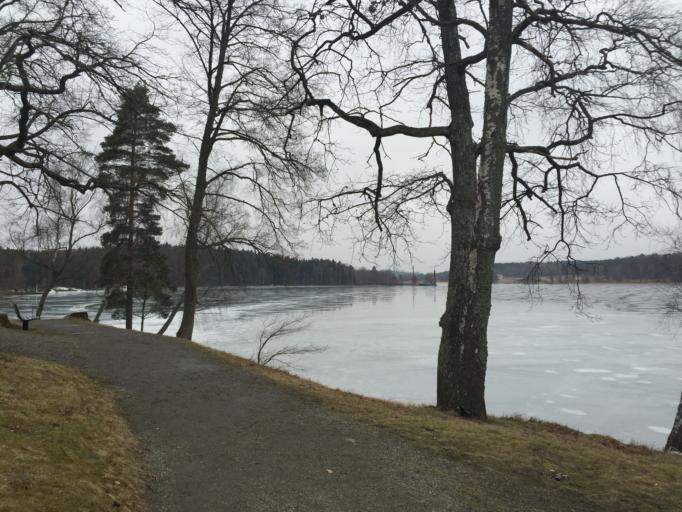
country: SE
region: Soedermanland
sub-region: Strangnas Kommun
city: Mariefred
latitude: 59.2477
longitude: 17.3090
